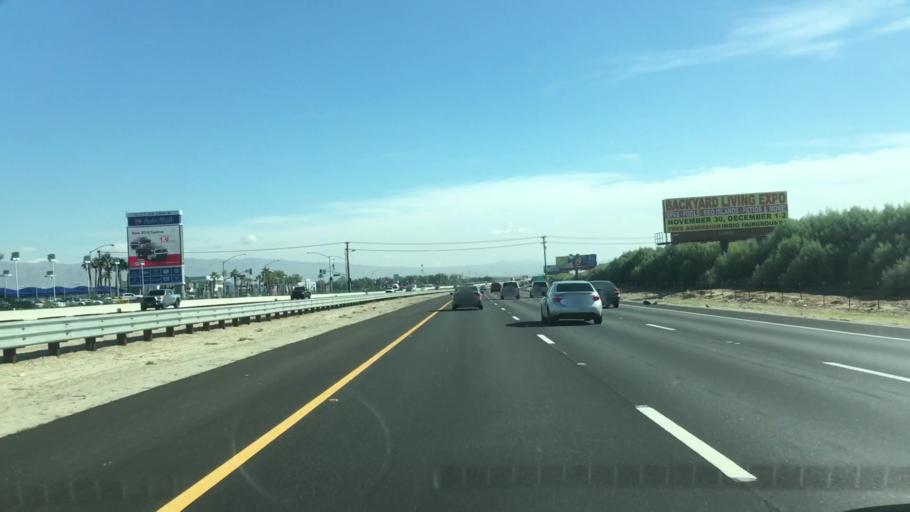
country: US
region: California
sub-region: Riverside County
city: Bermuda Dunes
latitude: 33.7560
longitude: -116.2889
